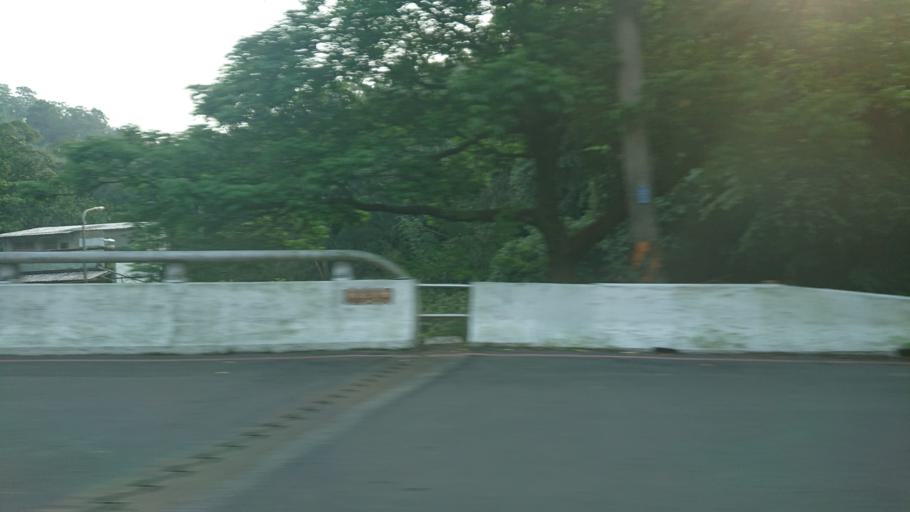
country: TW
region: Taiwan
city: Daxi
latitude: 24.8698
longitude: 121.4119
